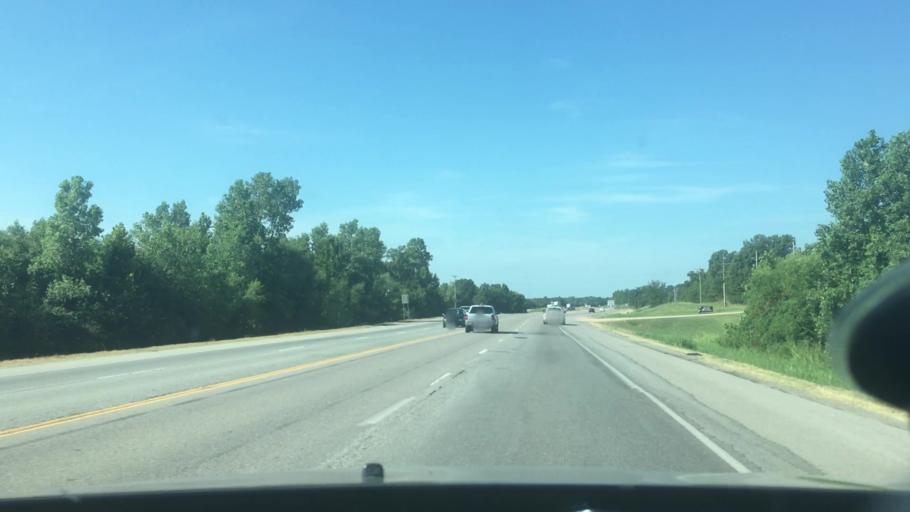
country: US
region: Oklahoma
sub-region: Atoka County
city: Atoka
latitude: 34.3147
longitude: -96.1709
